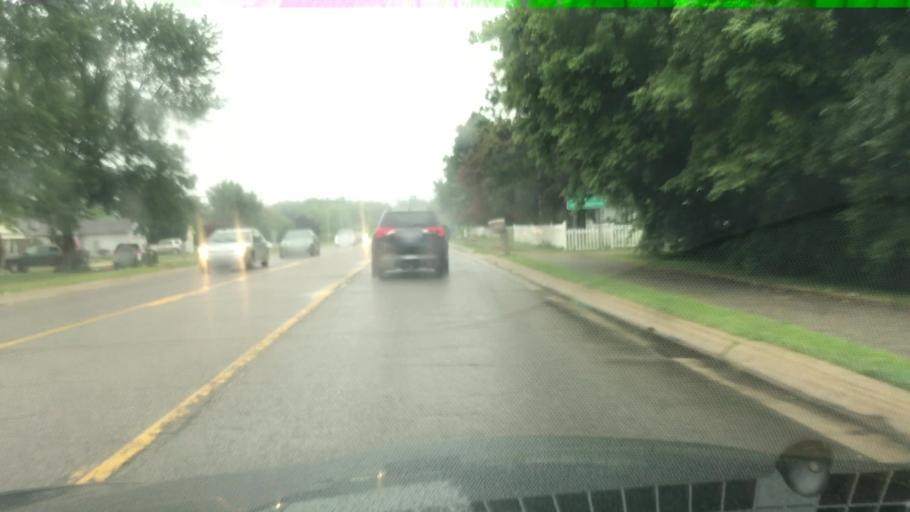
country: US
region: Michigan
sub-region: Oakland County
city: Auburn Hills
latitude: 42.7262
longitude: -83.2870
